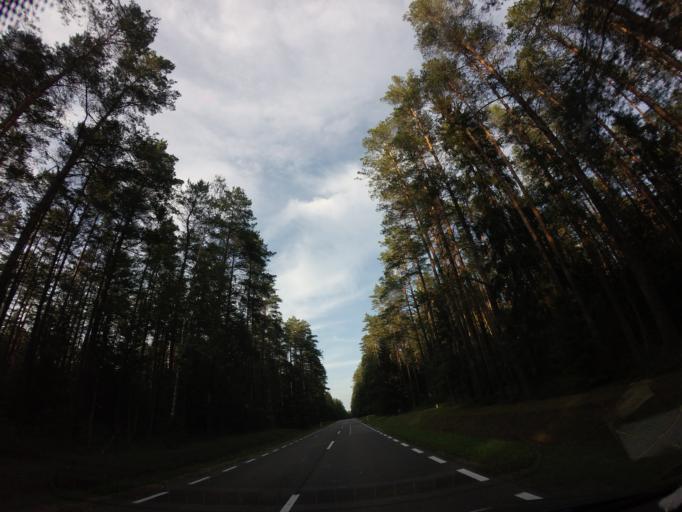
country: PL
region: Podlasie
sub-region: Powiat sejnenski
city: Krasnopol
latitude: 53.9702
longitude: 23.2528
